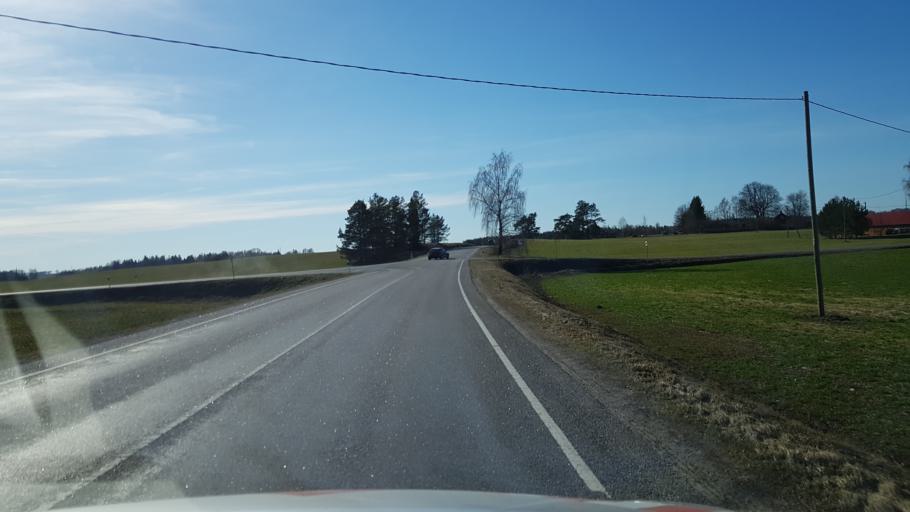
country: EE
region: Laeaene-Virumaa
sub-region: Vinni vald
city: Vinni
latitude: 59.3146
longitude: 26.4510
